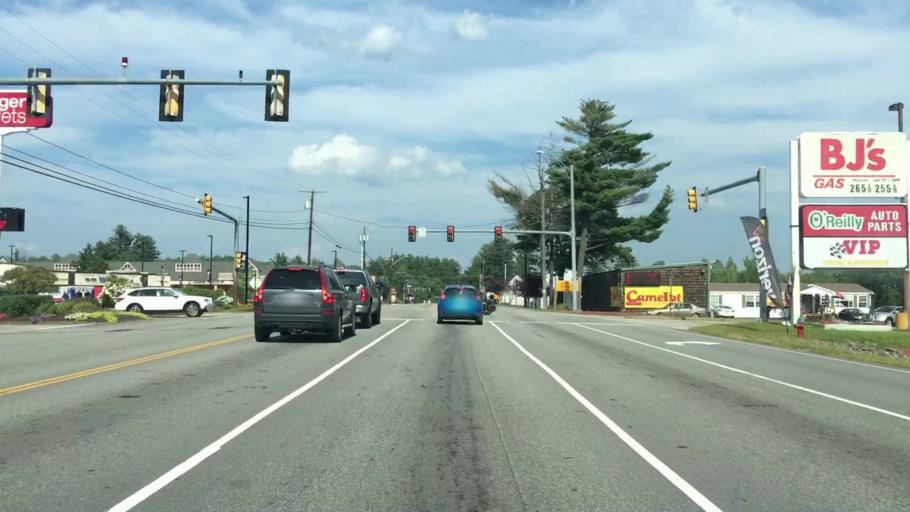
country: US
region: New Hampshire
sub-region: Belknap County
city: Tilton
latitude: 43.4577
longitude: -71.5619
